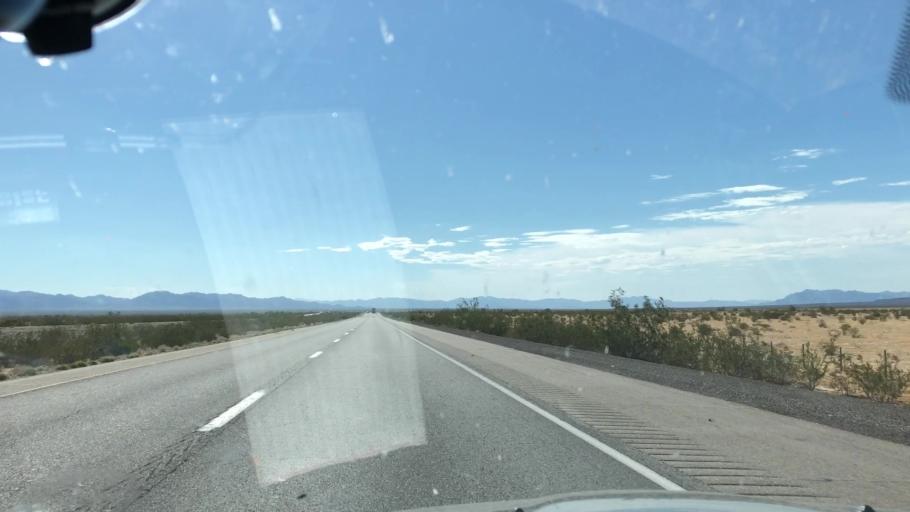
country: US
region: California
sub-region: Riverside County
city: Mesa Verde
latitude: 33.6224
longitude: -115.0406
